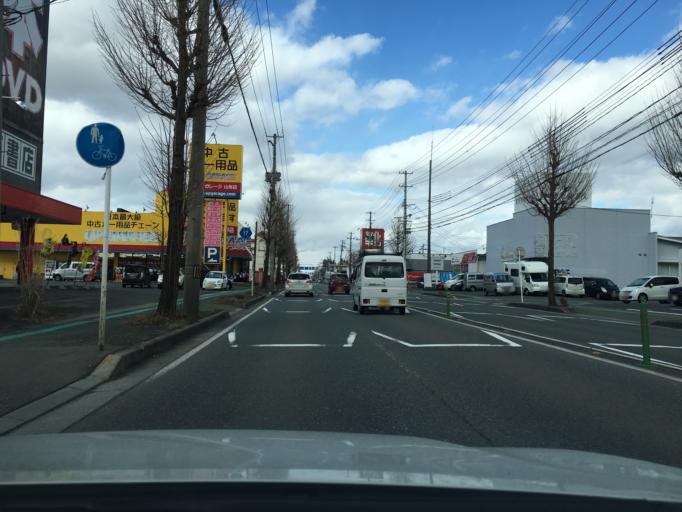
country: JP
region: Yamagata
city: Yamagata-shi
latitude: 38.2408
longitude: 140.3072
